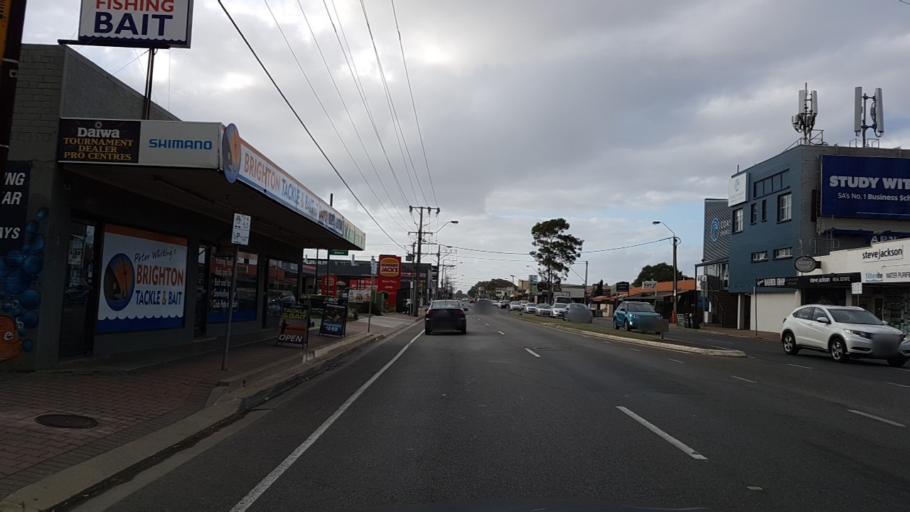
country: AU
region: South Australia
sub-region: Adelaide
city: Brighton
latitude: -35.0235
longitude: 138.5234
